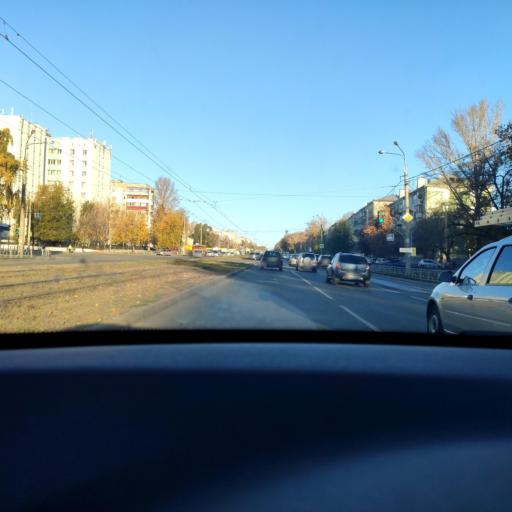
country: RU
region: Samara
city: Samara
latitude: 53.2087
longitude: 50.2326
